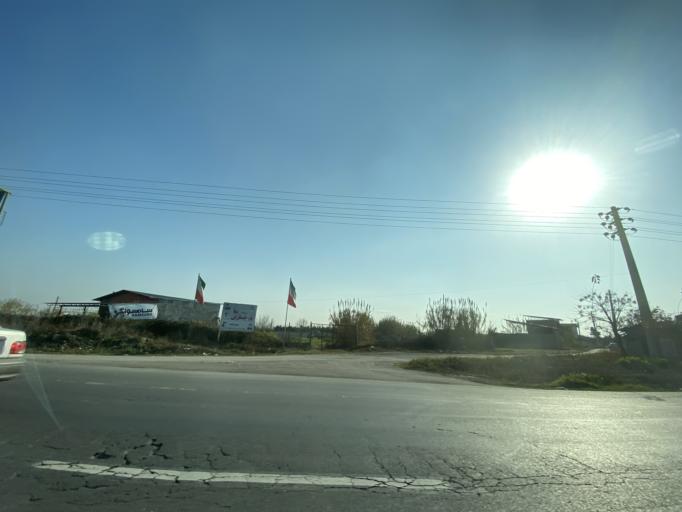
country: IR
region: Mazandaran
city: Babol
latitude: 36.5197
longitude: 52.5915
